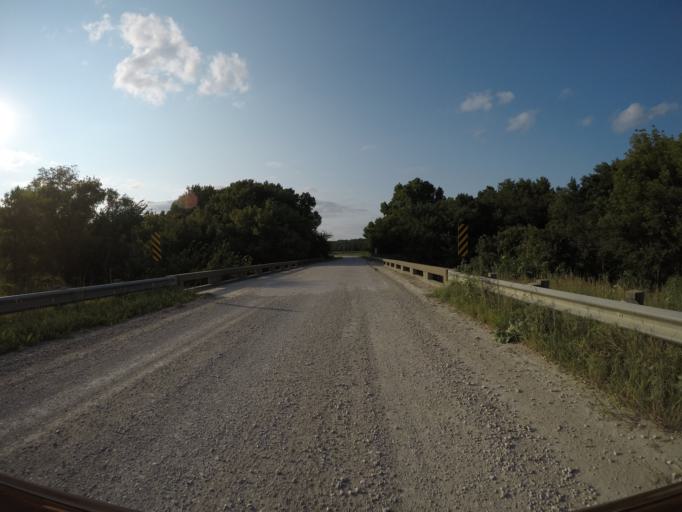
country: US
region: Kansas
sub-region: Wabaunsee County
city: Alma
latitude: 38.9492
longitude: -96.2418
